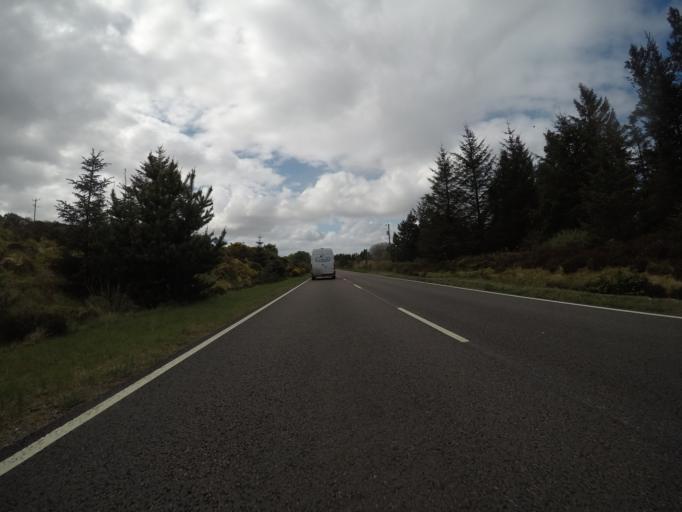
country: GB
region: Scotland
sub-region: Highland
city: Portree
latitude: 57.2544
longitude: -5.8116
